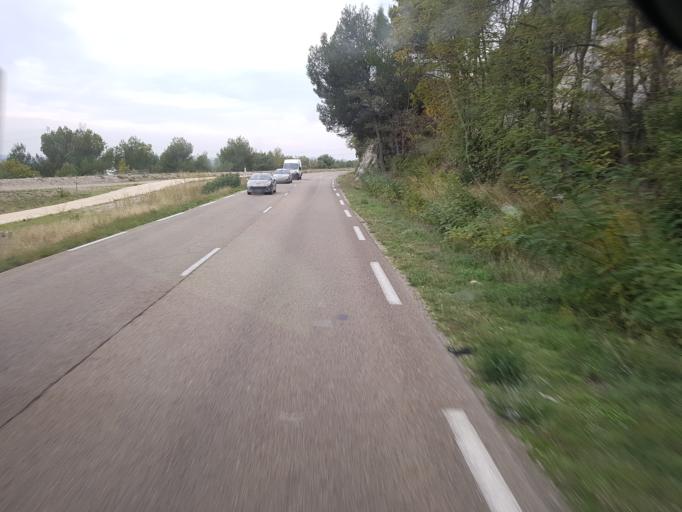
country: FR
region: Provence-Alpes-Cote d'Azur
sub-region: Departement des Bouches-du-Rhone
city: Barbentane
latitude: 43.9314
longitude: 4.7432
